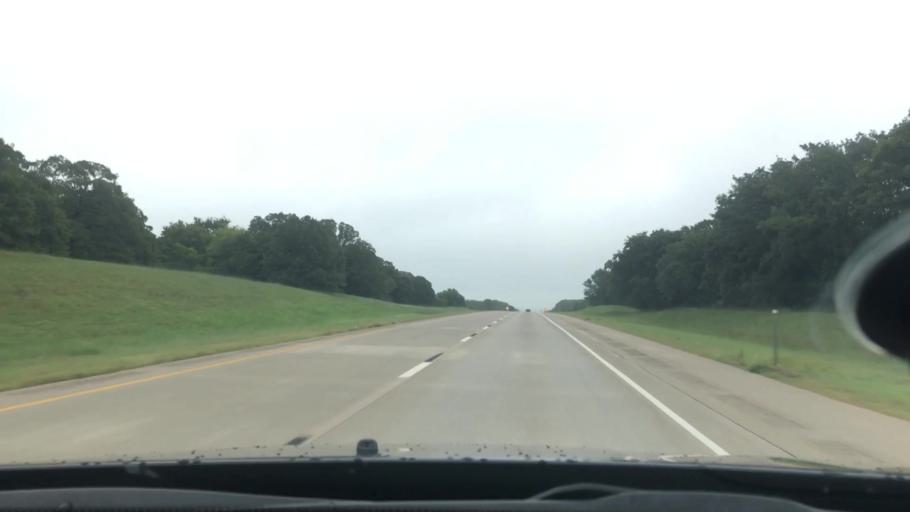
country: US
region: Oklahoma
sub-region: Okfuskee County
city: Boley
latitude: 35.3842
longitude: -96.5732
